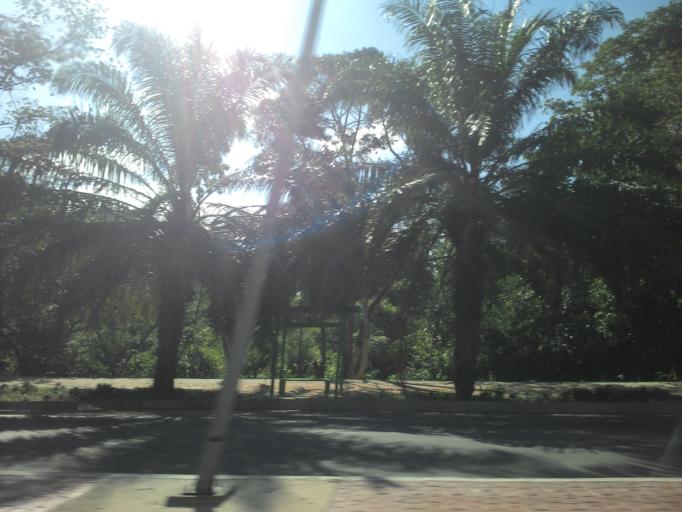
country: MX
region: Chiapas
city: Palenque
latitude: 17.5286
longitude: -91.9921
